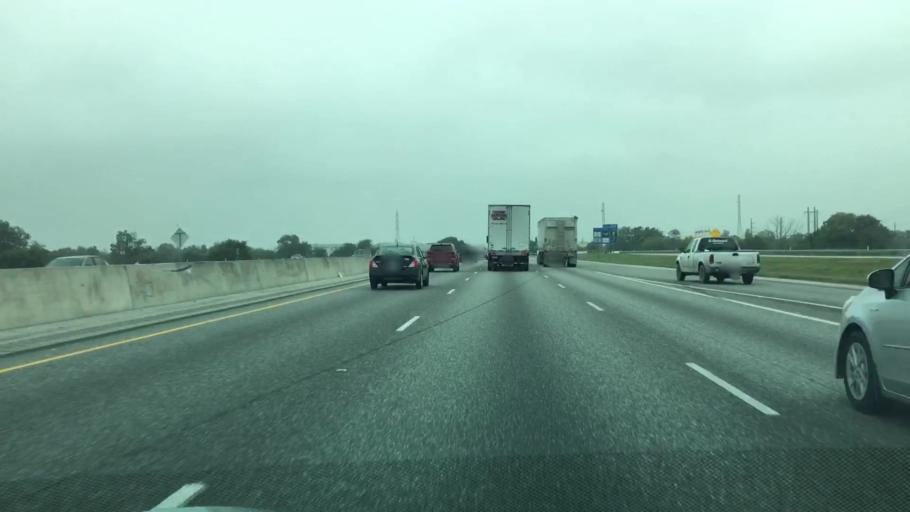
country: US
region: Texas
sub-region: Hays County
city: San Marcos
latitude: 29.9161
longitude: -97.8963
